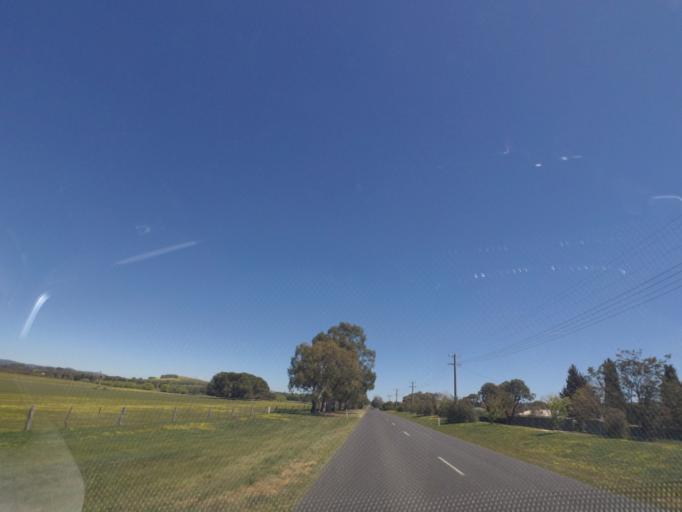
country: AU
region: Victoria
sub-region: Hume
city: Sunbury
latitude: -37.2792
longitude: 144.7193
